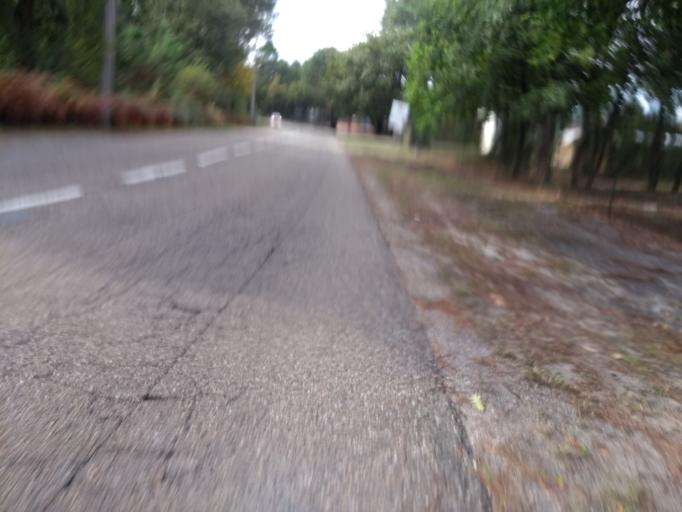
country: FR
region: Aquitaine
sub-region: Departement de la Gironde
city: Cestas
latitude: 44.7498
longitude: -0.6898
